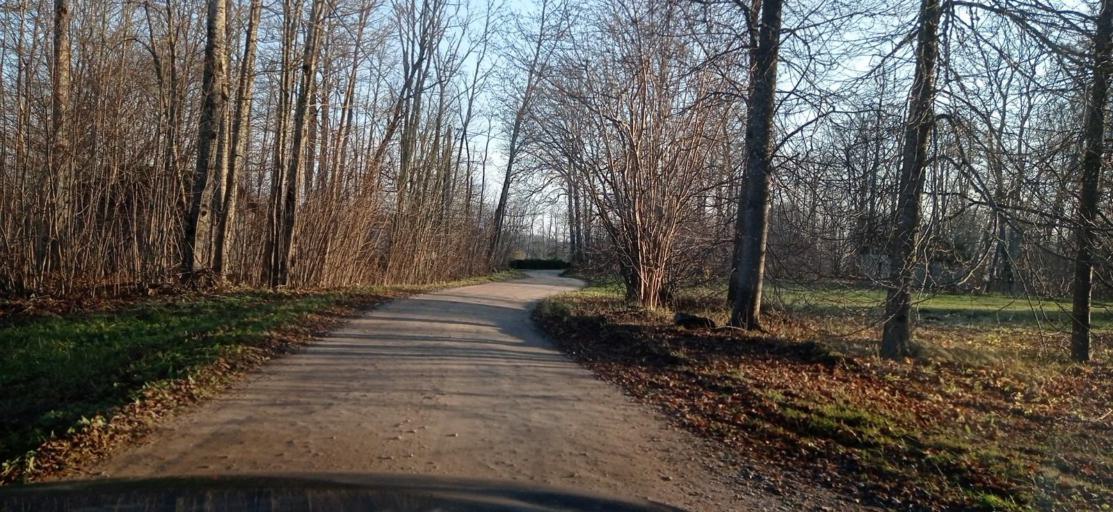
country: EE
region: Jogevamaa
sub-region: Tabivere vald
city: Tabivere
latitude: 58.6724
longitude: 26.7603
